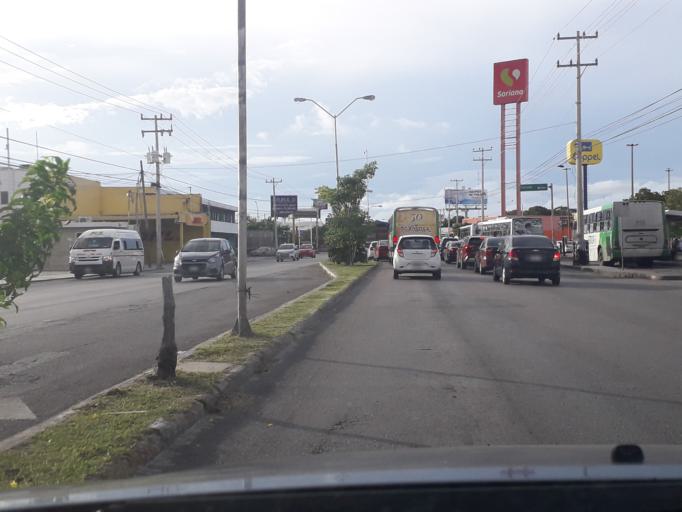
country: MX
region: Yucatan
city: Merida
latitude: 20.9888
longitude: -89.6623
